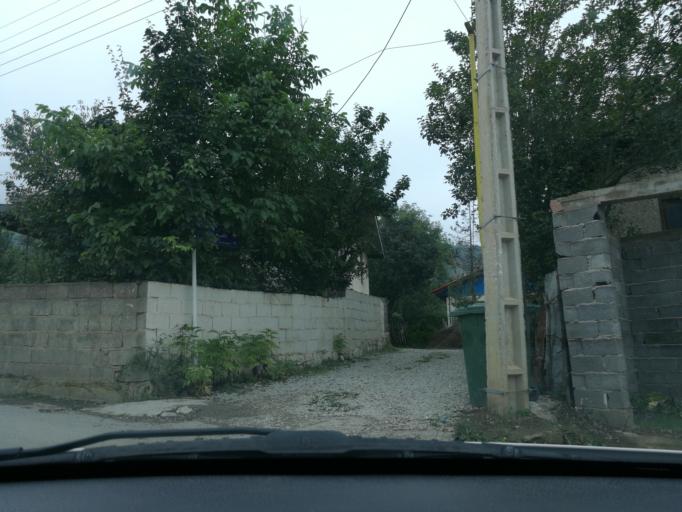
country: IR
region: Mazandaran
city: `Abbasabad
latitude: 36.4951
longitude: 51.2085
